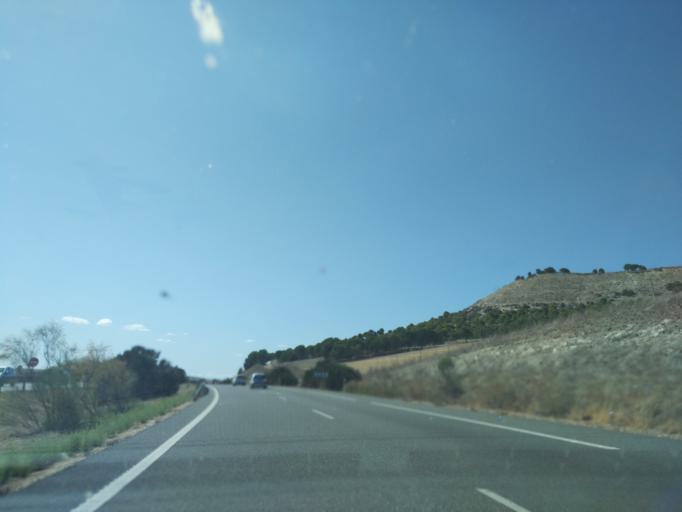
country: ES
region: Castille and Leon
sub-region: Provincia de Valladolid
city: Marzales
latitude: 41.6086
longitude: -5.1440
